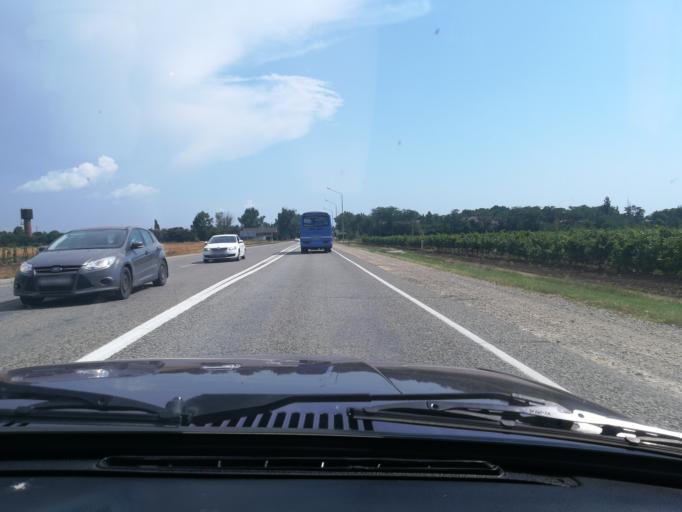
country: RU
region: Krasnodarskiy
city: Vinogradnyy
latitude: 45.0675
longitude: 37.3185
